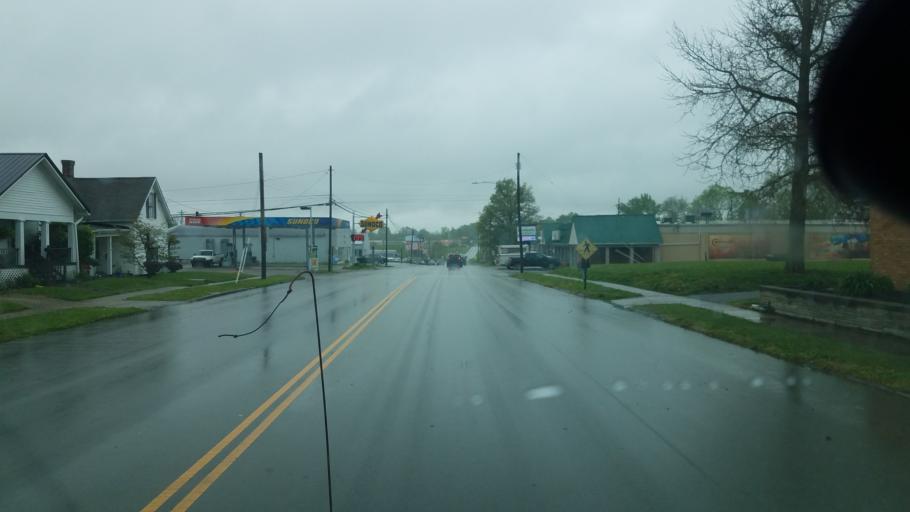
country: US
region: Ohio
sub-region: Highland County
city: Greenfield
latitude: 39.3488
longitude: -83.3958
